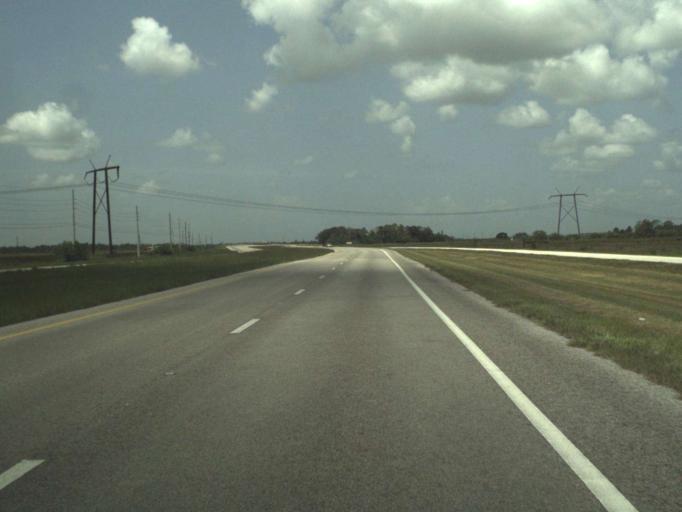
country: US
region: Florida
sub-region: Saint Lucie County
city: Fort Pierce South
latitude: 27.3853
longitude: -80.4669
